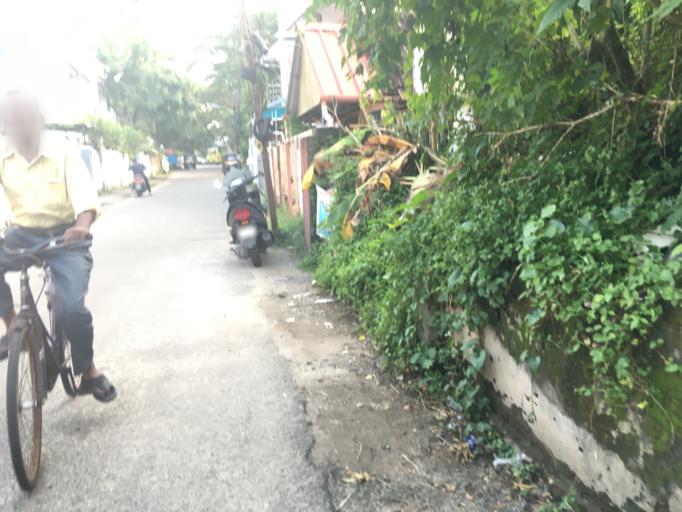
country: IN
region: Kerala
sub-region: Ernakulam
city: Cochin
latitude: 9.9558
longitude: 76.2406
